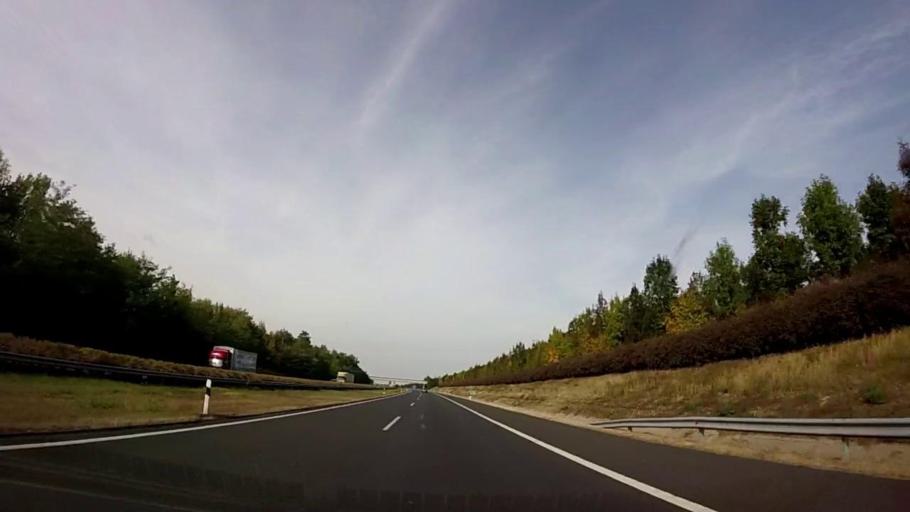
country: HU
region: Somogy
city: Balatonszarszo
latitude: 46.7919
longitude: 17.7711
